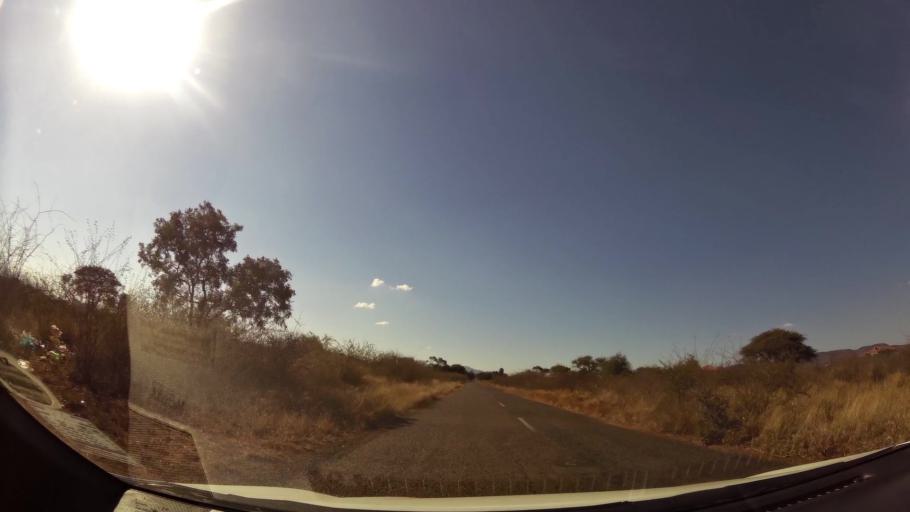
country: ZA
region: Limpopo
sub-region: Waterberg District Municipality
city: Mokopane
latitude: -24.2037
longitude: 28.9921
